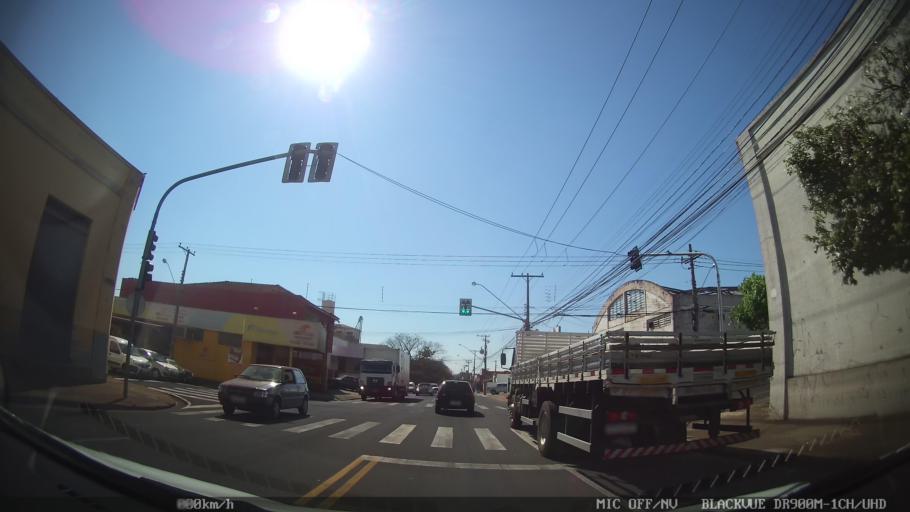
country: BR
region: Sao Paulo
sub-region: Sao Jose Do Rio Preto
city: Sao Jose do Rio Preto
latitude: -20.7999
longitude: -49.3957
